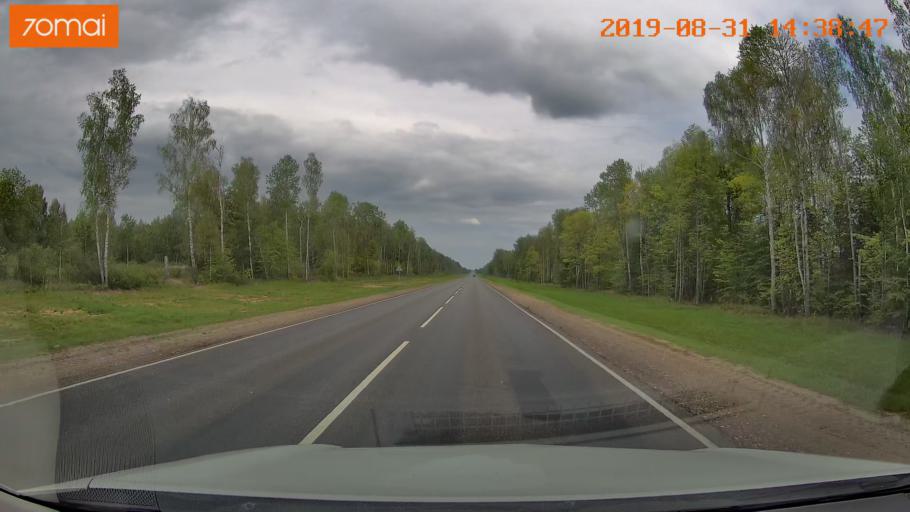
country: RU
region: Smolensk
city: Yekimovichi
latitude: 54.1869
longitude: 33.5367
